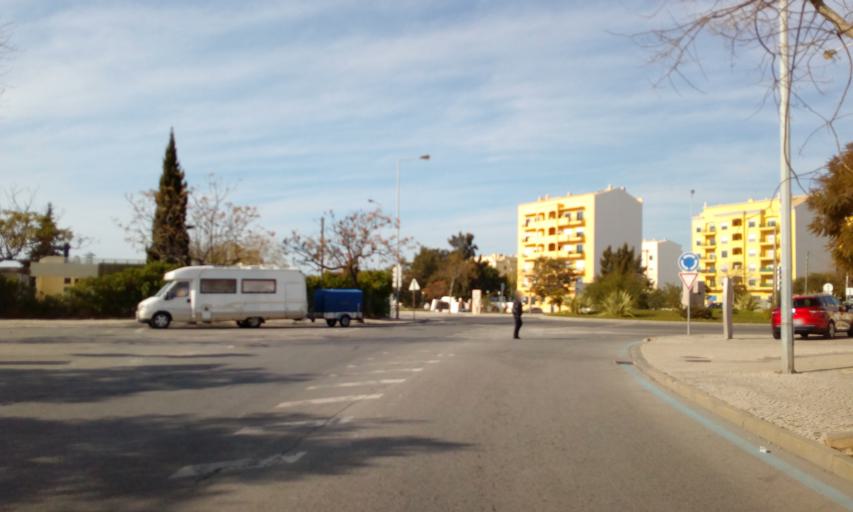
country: PT
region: Faro
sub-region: Faro
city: Faro
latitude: 37.0134
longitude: -7.9257
